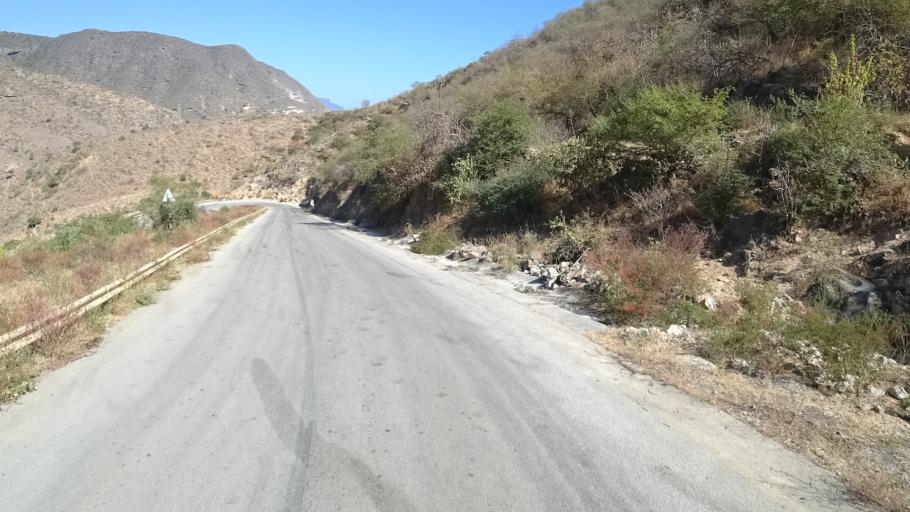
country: YE
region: Al Mahrah
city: Hawf
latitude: 16.7473
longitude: 53.4113
